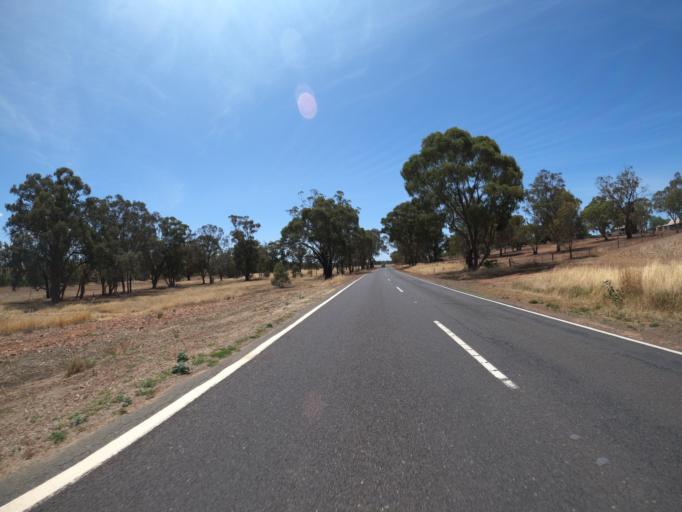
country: AU
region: Victoria
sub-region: Benalla
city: Benalla
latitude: -36.3346
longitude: 145.9595
